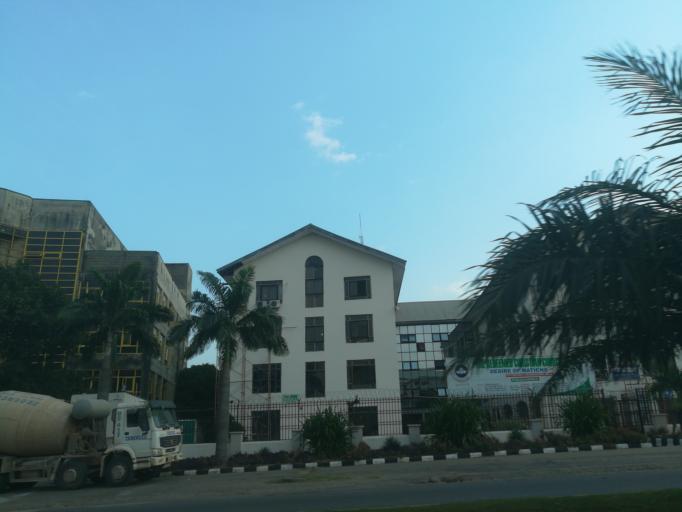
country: NG
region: Abuja Federal Capital Territory
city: Abuja
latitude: 9.0646
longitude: 7.4276
